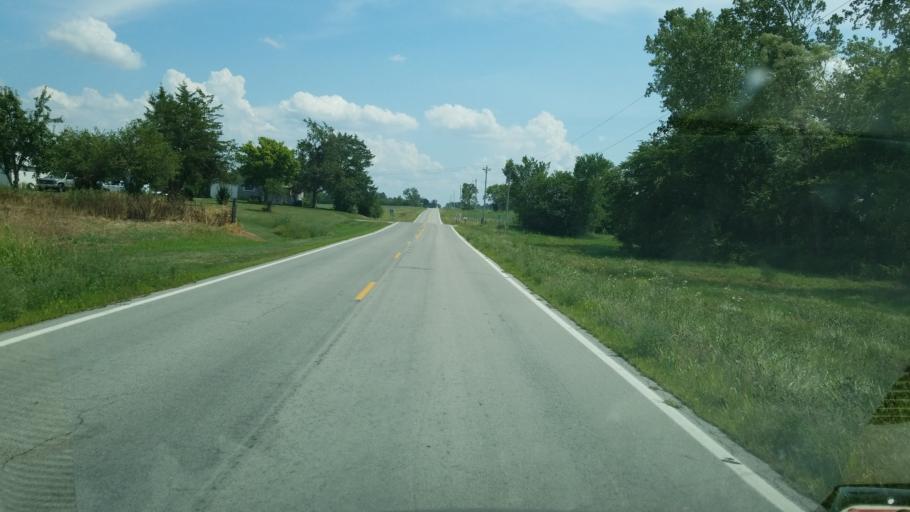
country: US
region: Ohio
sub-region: Hardin County
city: Forest
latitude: 40.7387
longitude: -83.4309
